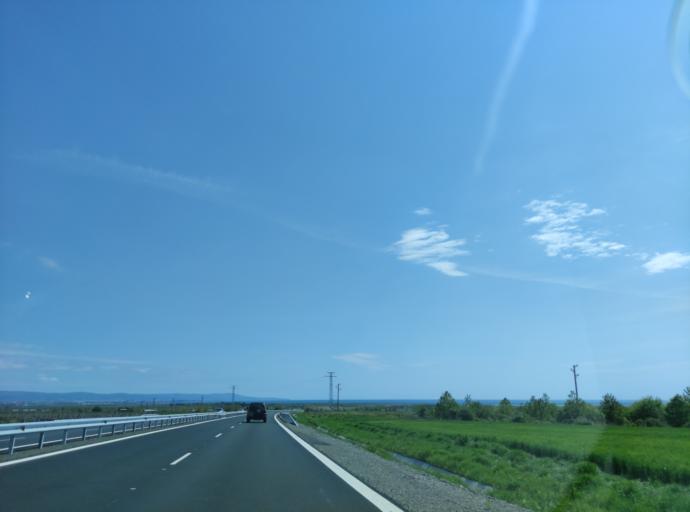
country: BG
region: Burgas
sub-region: Obshtina Pomorie
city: Pomorie
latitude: 42.5860
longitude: 27.5901
